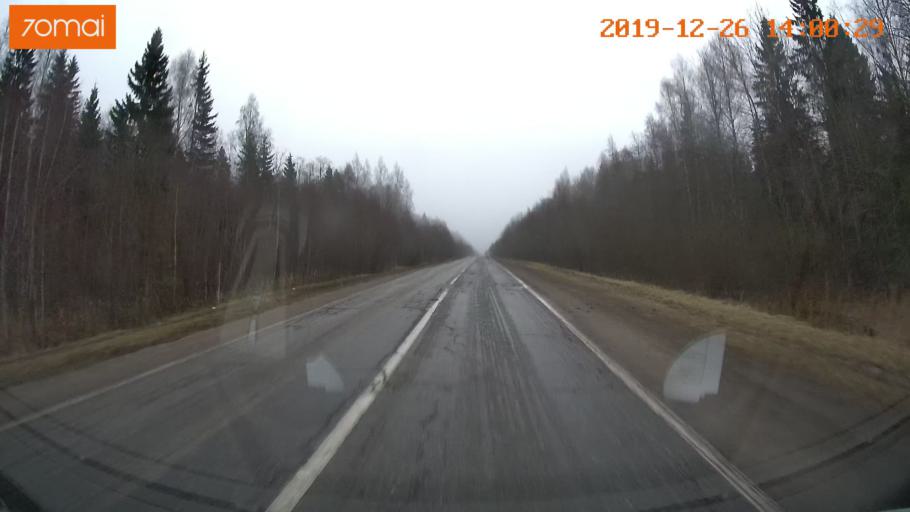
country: RU
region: Jaroslavl
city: Poshekhon'ye
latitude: 58.5578
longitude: 38.7442
